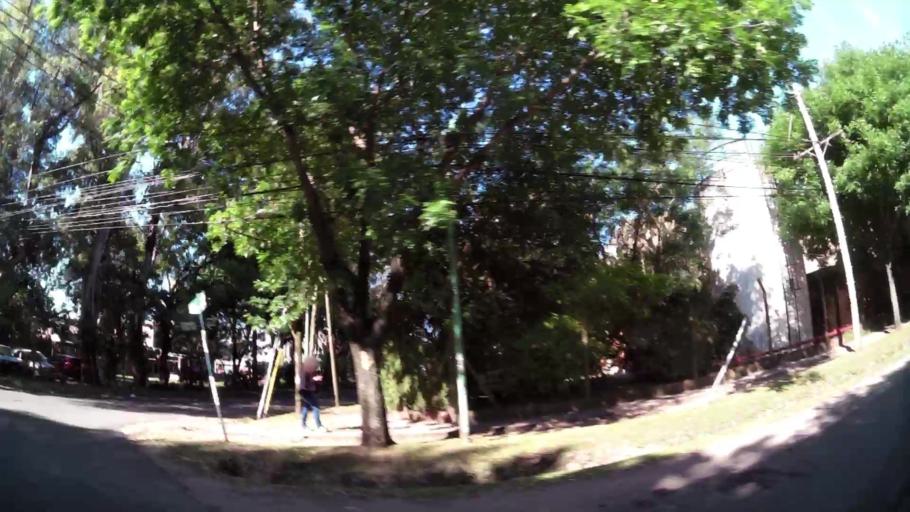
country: AR
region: Buenos Aires
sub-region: Partido de Tigre
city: Tigre
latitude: -34.4805
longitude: -58.6606
